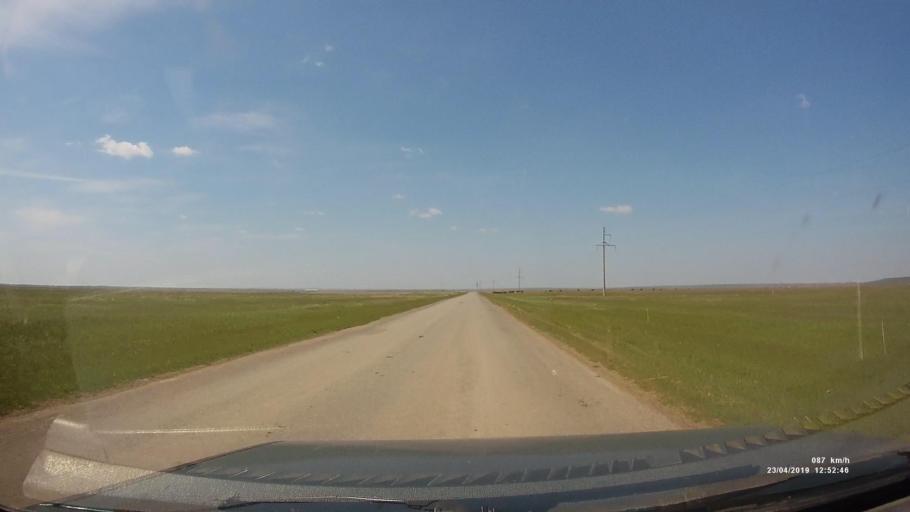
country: RU
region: Kalmykiya
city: Yashalta
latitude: 46.5678
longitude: 42.6053
